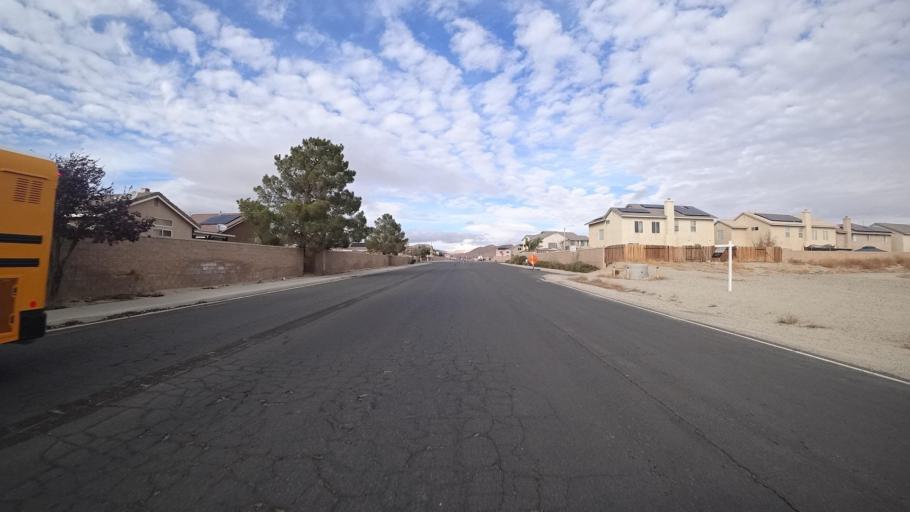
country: US
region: California
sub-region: Kern County
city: Rosamond
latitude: 34.8555
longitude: -118.1937
